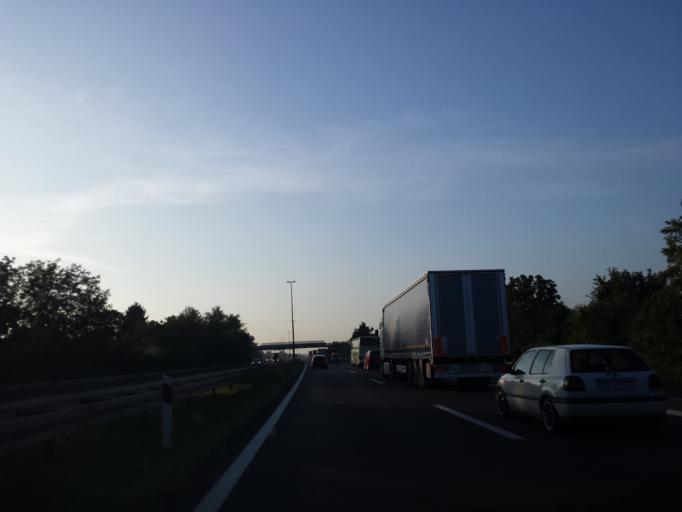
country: HR
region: Grad Zagreb
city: Lucko
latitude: 45.7674
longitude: 15.8910
